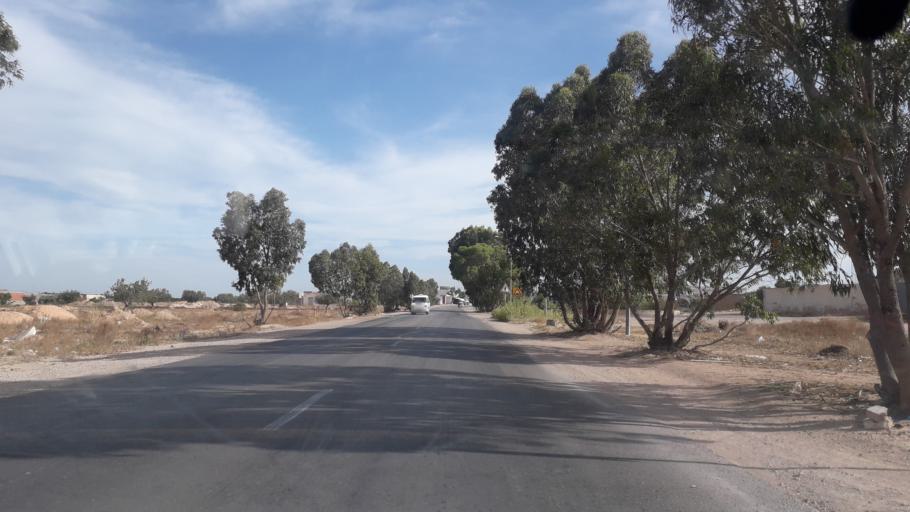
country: TN
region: Safaqis
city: Al Qarmadah
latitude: 34.8885
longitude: 10.7626
